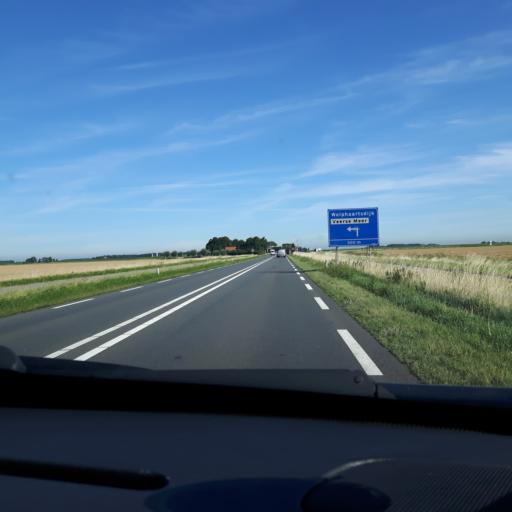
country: NL
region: Zeeland
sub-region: Gemeente Goes
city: Goes
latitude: 51.5260
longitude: 3.8683
